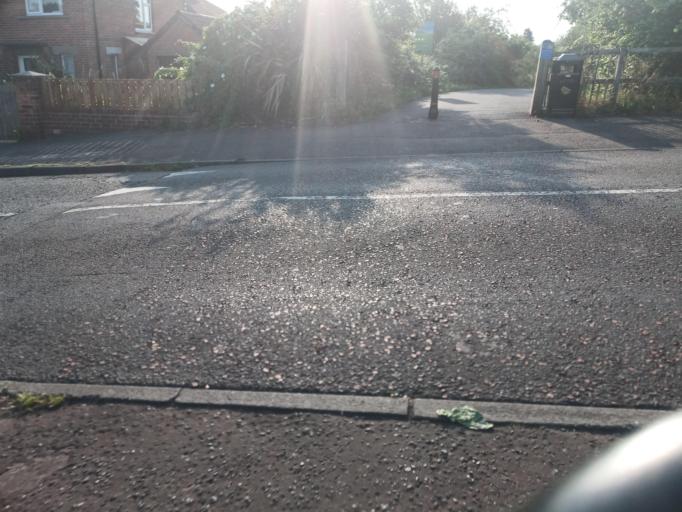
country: GB
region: Northern Ireland
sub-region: Castlereagh District
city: Dundonald
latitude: 54.5911
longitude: -5.8370
